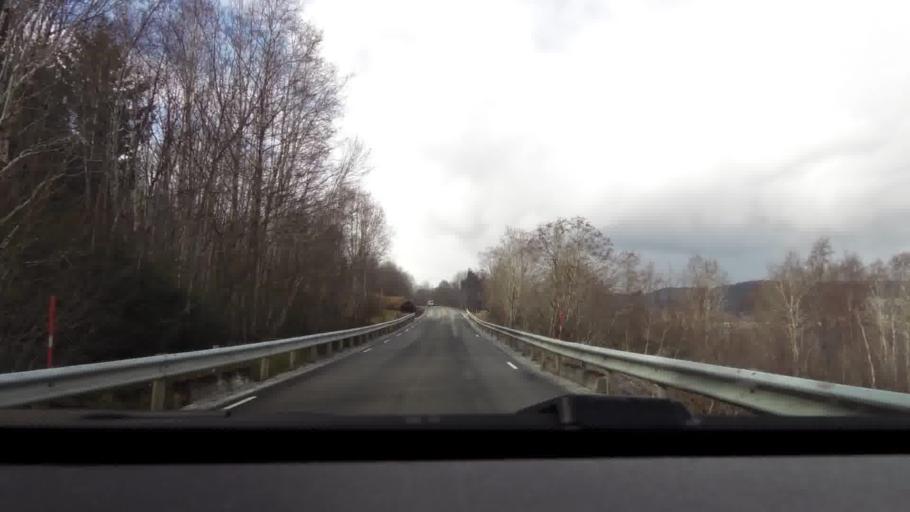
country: NO
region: More og Romsdal
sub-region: Gjemnes
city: Batnfjordsora
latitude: 62.9678
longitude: 7.7282
